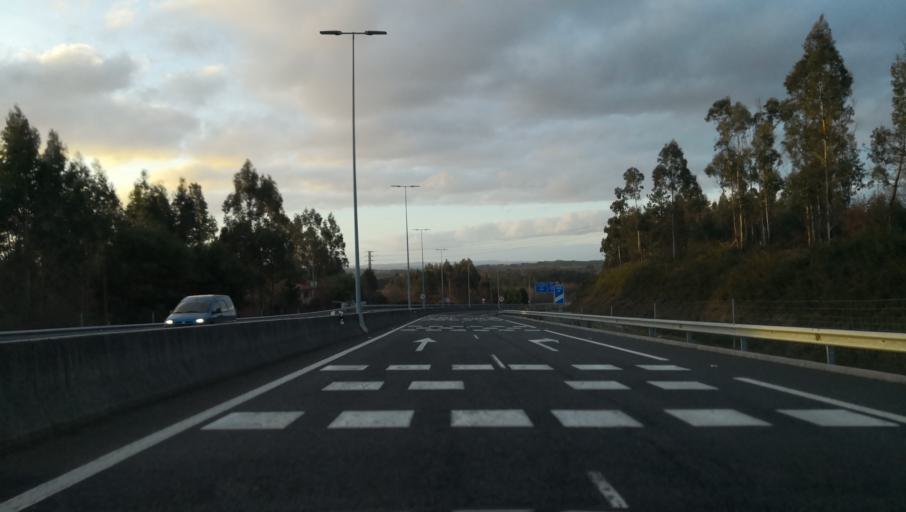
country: ES
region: Galicia
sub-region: Provincia da Coruna
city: Oroso
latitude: 42.9066
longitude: -8.4302
